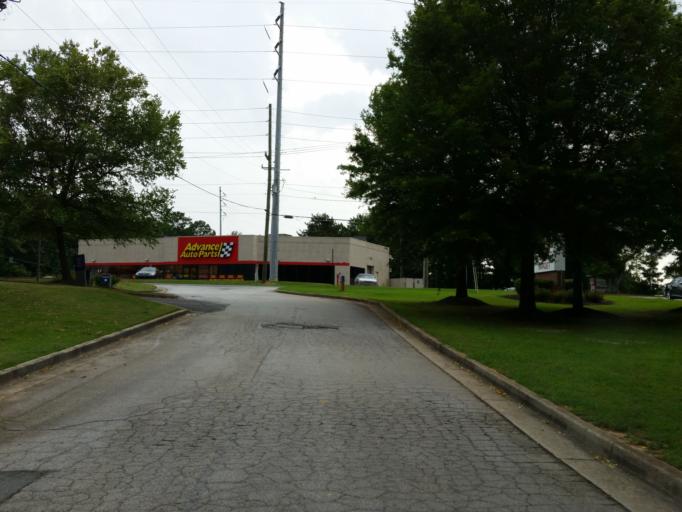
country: US
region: Georgia
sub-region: Fulton County
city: Sandy Springs
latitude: 33.9832
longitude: -84.4295
